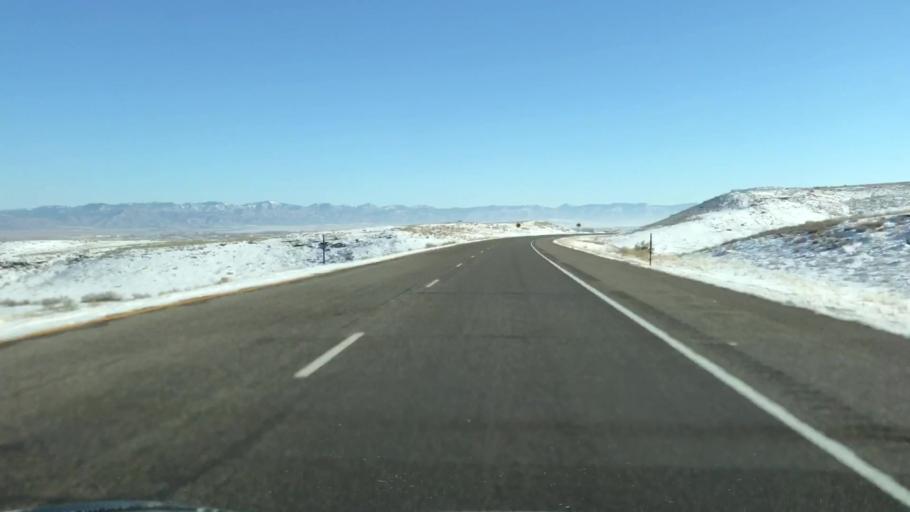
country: US
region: Colorado
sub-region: Mesa County
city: Loma
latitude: 39.2291
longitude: -108.9152
